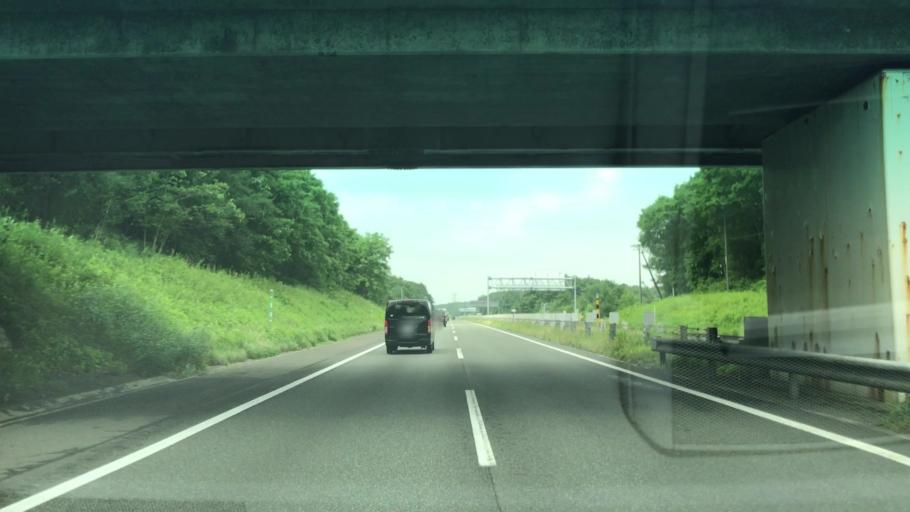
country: JP
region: Hokkaido
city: Tomakomai
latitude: 42.7171
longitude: 141.6524
